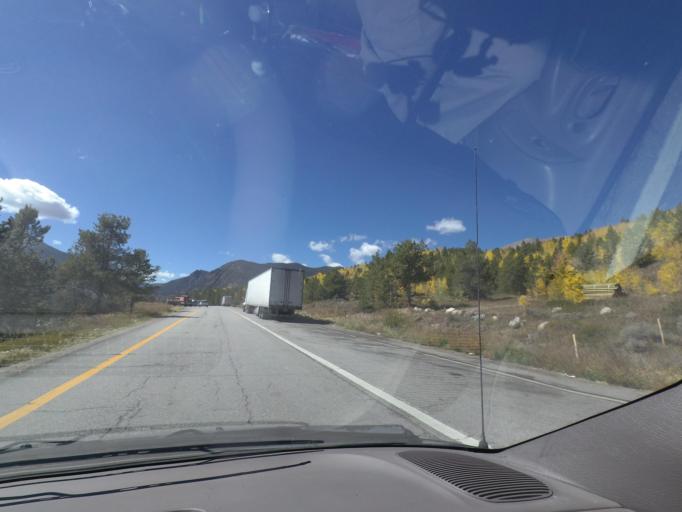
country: US
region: Colorado
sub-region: Summit County
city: Frisco
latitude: 39.6021
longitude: -106.0882
